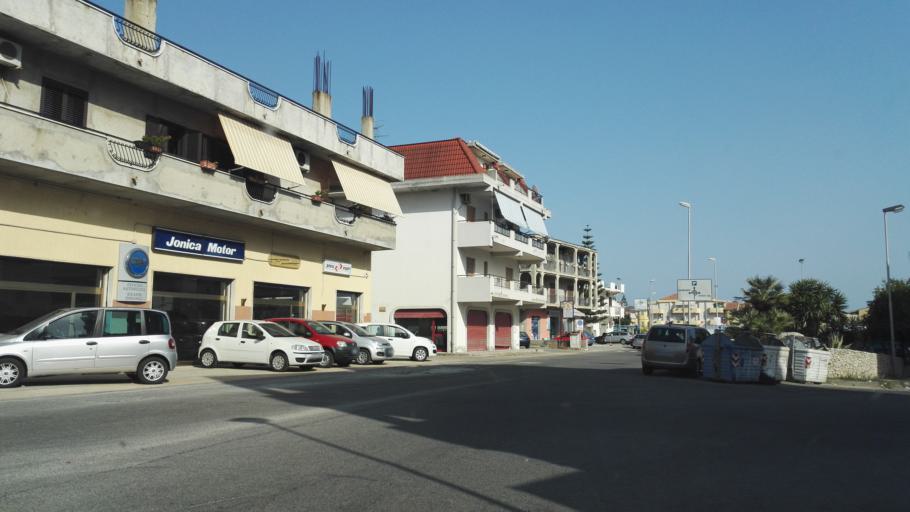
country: IT
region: Calabria
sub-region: Provincia di Reggio Calabria
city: Caulonia Marina
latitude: 38.3456
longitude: 16.4668
